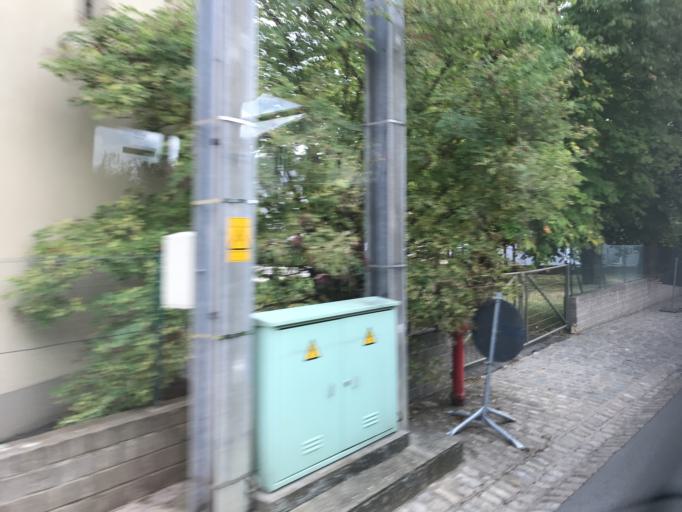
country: LU
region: Luxembourg
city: Crauthem
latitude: 49.5231
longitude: 6.1273
